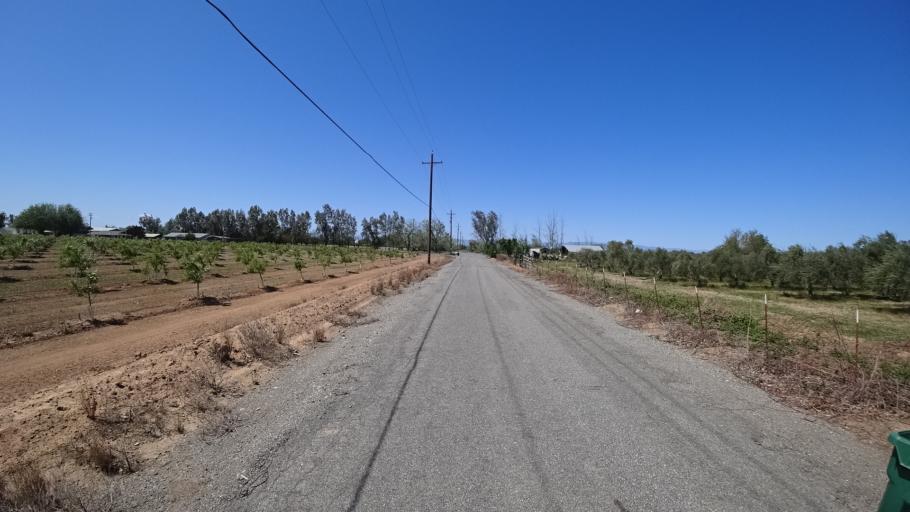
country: US
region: California
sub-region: Glenn County
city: Orland
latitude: 39.7892
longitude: -122.2011
